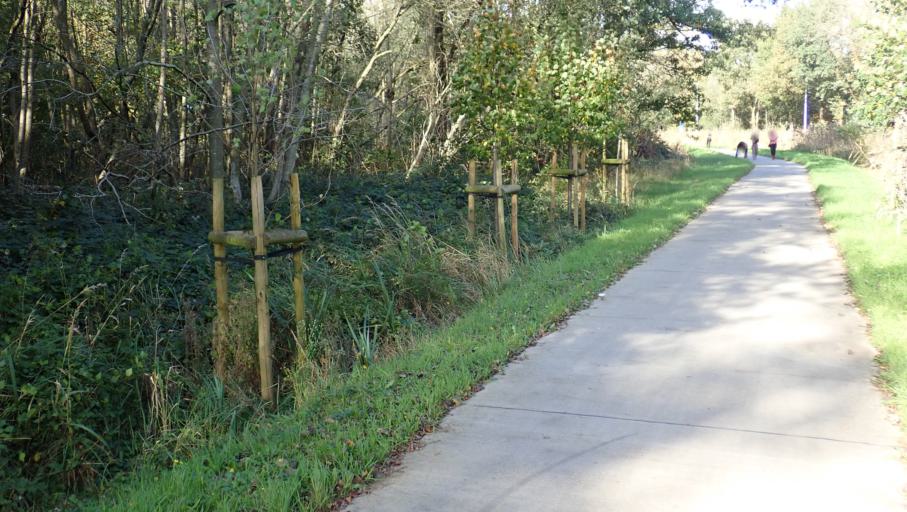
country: BE
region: Flanders
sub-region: Provincie Oost-Vlaanderen
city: Stekene
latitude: 51.1711
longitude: 4.0048
